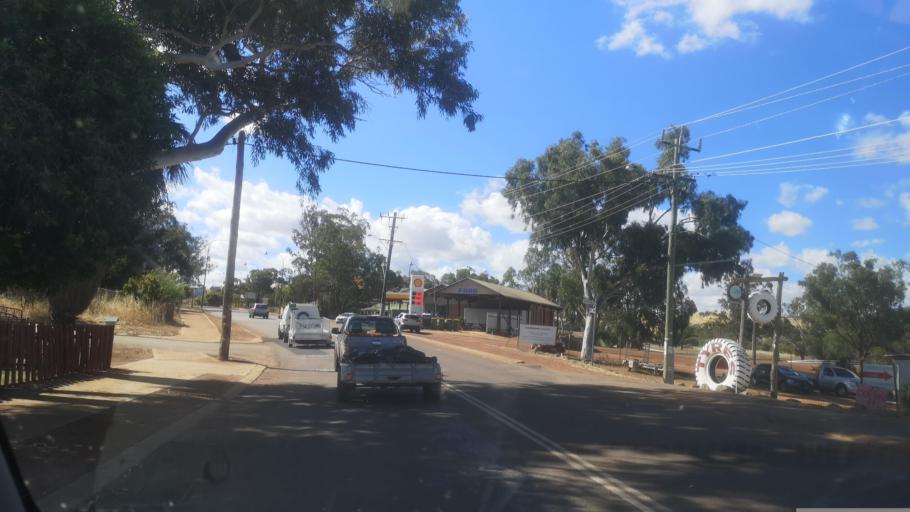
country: AU
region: Western Australia
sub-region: Toodyay
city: Toodyay
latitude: -31.5563
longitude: 116.4759
